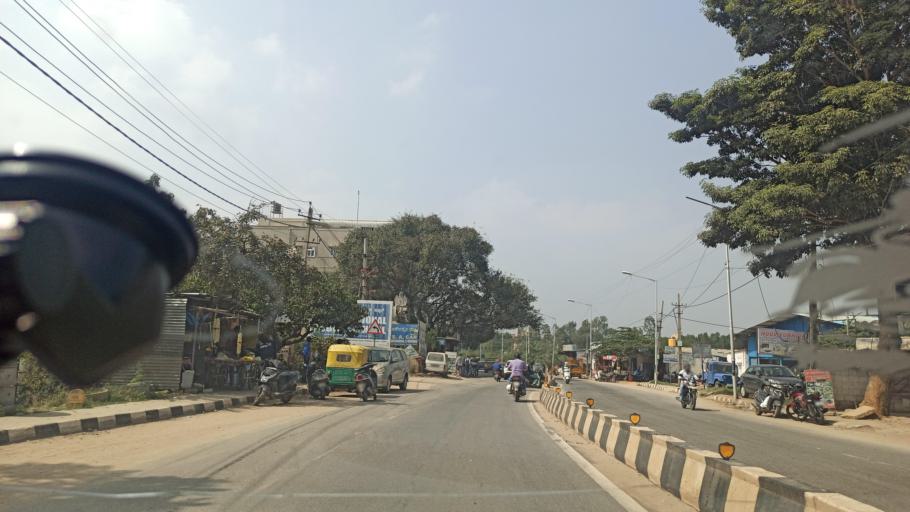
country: IN
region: Karnataka
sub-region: Bangalore Urban
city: Yelahanka
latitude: 13.1040
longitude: 77.6137
